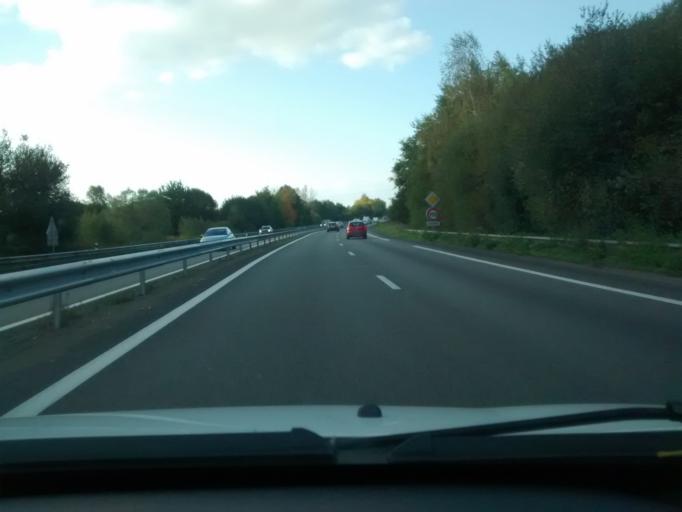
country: FR
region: Pays de la Loire
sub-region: Departement de la Loire-Atlantique
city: Orvault
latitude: 47.2809
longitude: -1.6030
